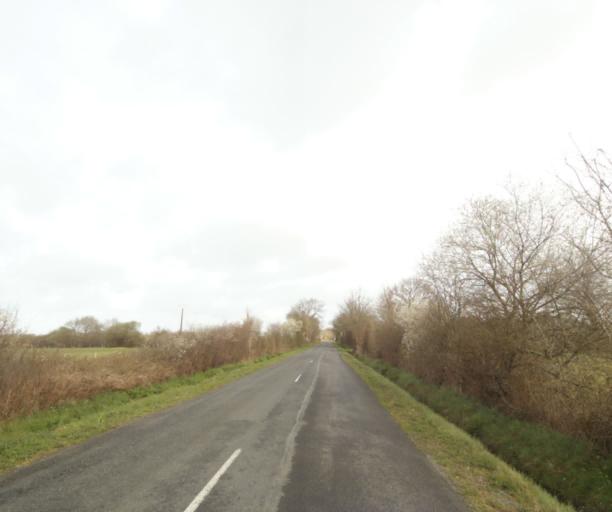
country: FR
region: Pays de la Loire
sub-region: Departement de la Loire-Atlantique
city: Bouvron
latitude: 47.3983
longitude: -1.8836
